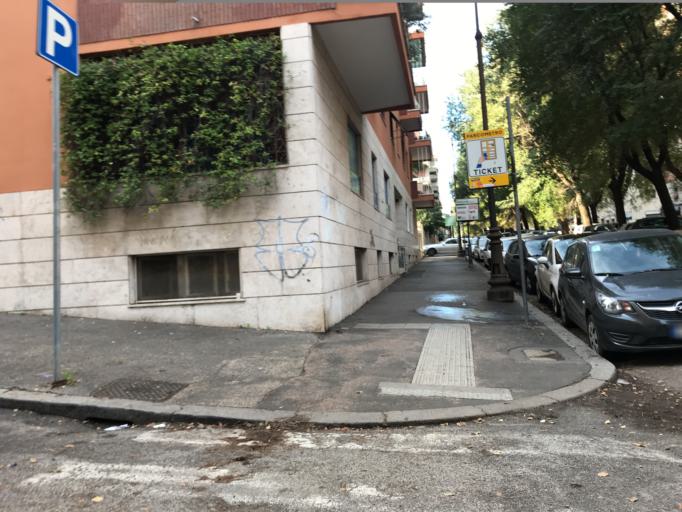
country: IT
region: Latium
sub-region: Citta metropolitana di Roma Capitale
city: Rome
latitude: 41.9085
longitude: 12.5190
